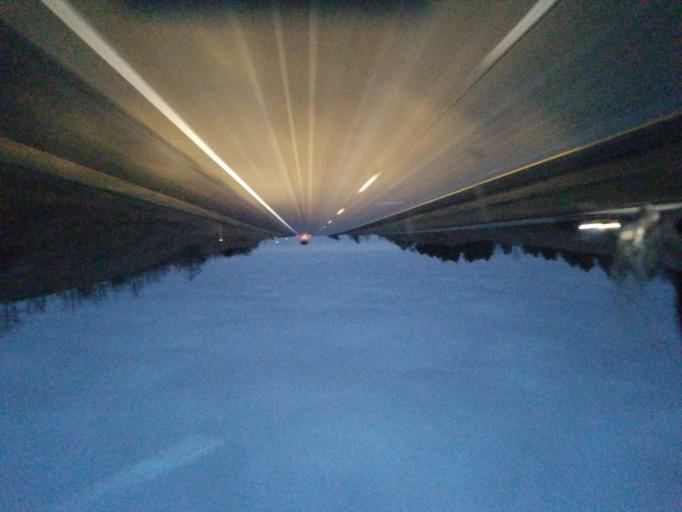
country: US
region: Iowa
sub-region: Cass County
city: Atlantic
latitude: 41.4969
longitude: -94.8216
